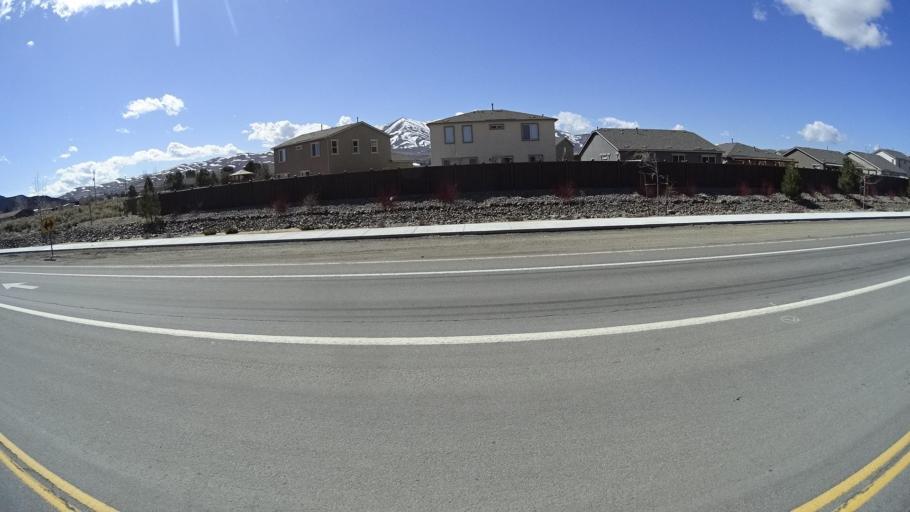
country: US
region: Nevada
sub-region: Washoe County
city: Lemmon Valley
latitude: 39.6381
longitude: -119.8590
